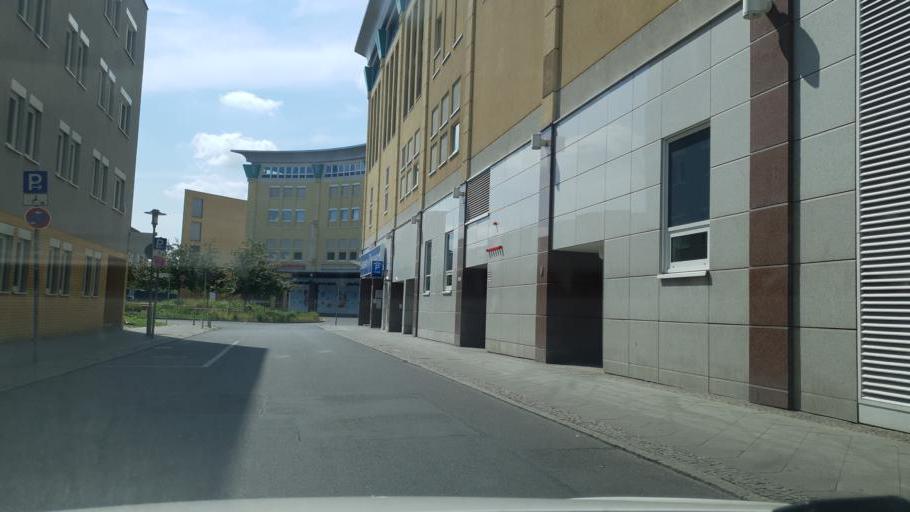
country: DE
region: Berlin
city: Hellersdorf
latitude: 52.5386
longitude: 13.6059
